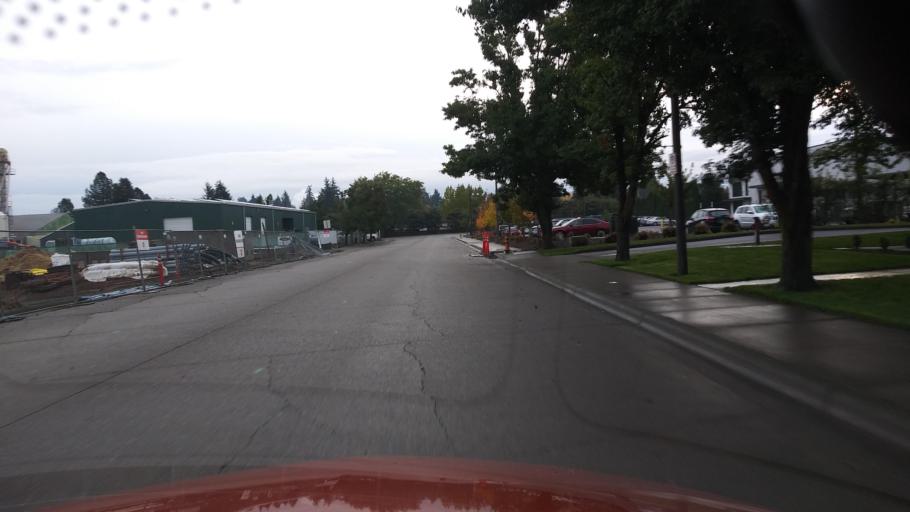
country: US
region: Oregon
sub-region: Washington County
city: Cornelius
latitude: 45.5265
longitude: -123.0617
